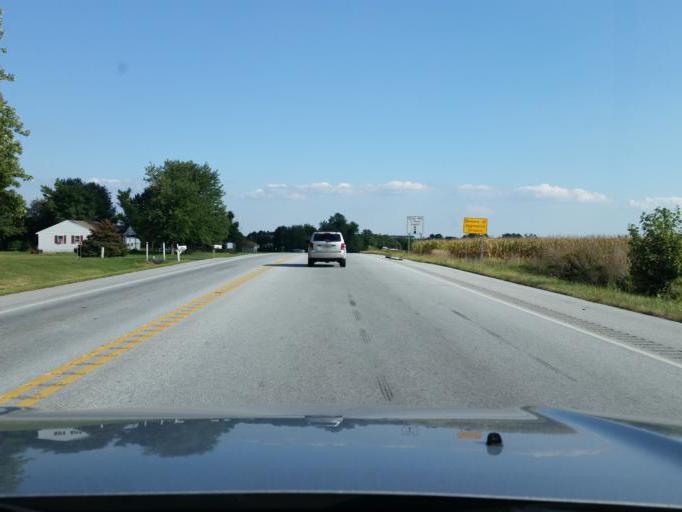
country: US
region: Pennsylvania
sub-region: Chester County
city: Atglen
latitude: 39.9345
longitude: -75.9553
